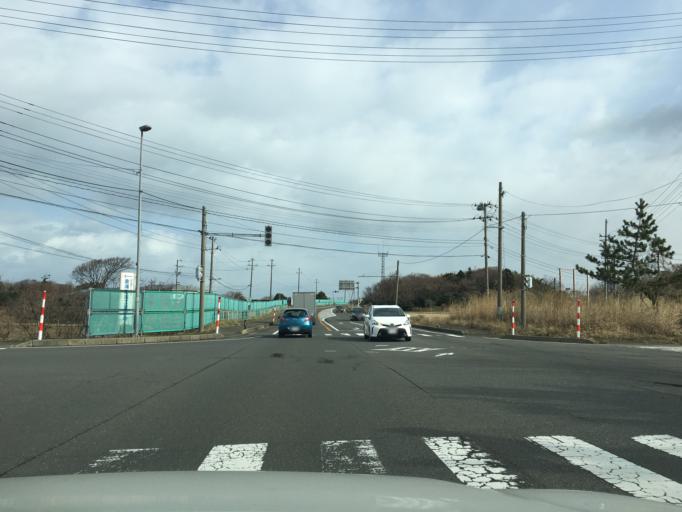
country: JP
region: Yamagata
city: Yuza
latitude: 39.2721
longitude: 139.9238
